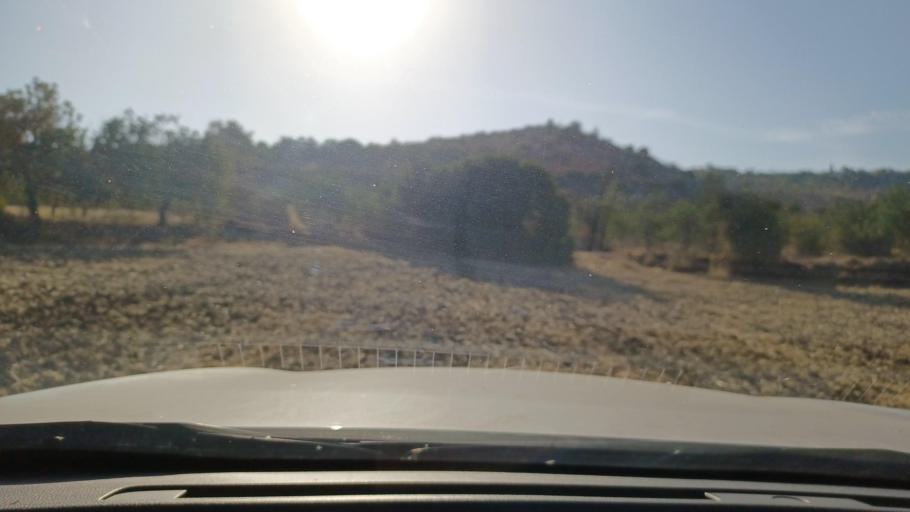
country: CY
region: Pafos
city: Polis
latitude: 35.0050
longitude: 32.5029
